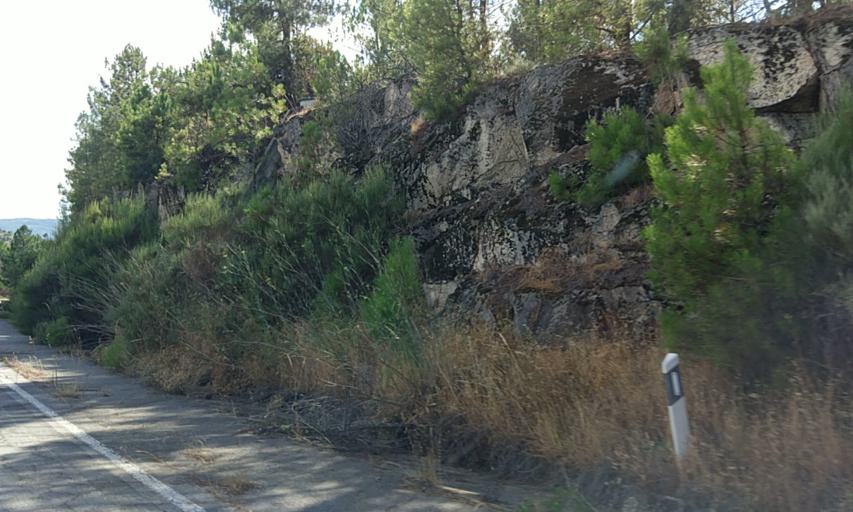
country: PT
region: Vila Real
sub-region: Sabrosa
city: Sabrosa
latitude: 41.3647
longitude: -7.5544
